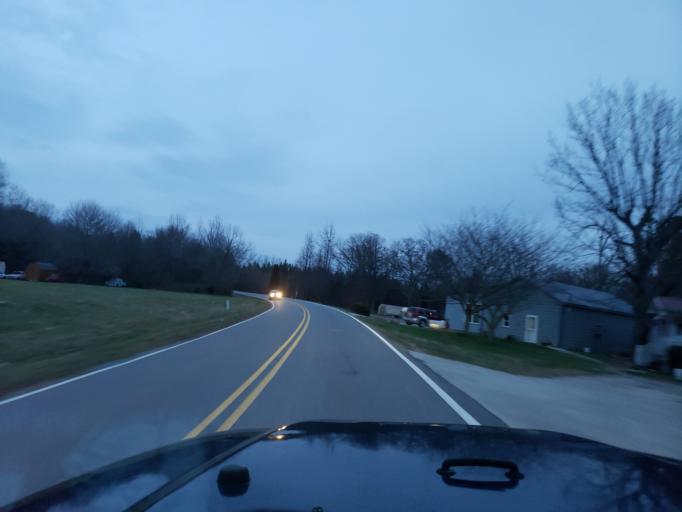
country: US
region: North Carolina
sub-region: Cleveland County
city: White Plains
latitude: 35.1848
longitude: -81.4289
